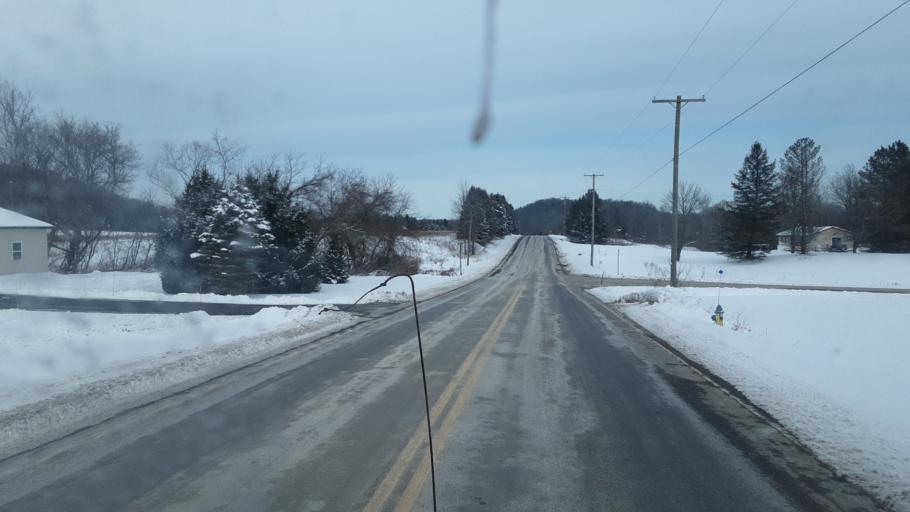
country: US
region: New York
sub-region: Wayne County
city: Newark
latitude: 43.0849
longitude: -77.0579
